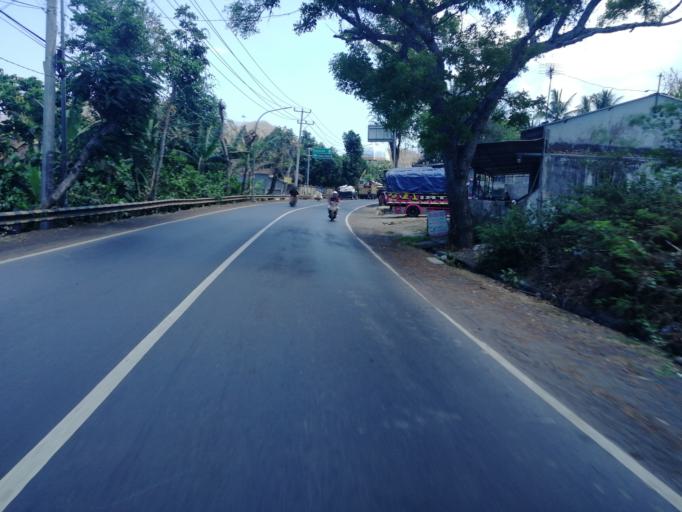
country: ID
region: West Nusa Tenggara
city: Jelateng Timur
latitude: -8.7202
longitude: 116.0738
